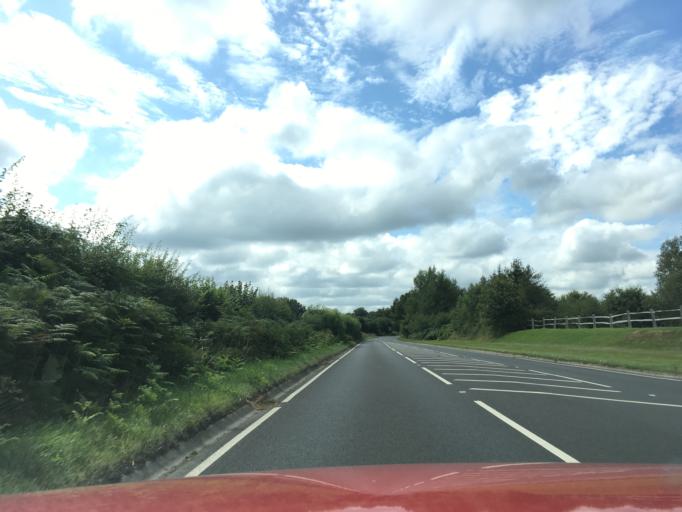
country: GB
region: England
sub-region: Kent
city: Edenbridge
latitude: 51.1330
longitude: 0.0912
